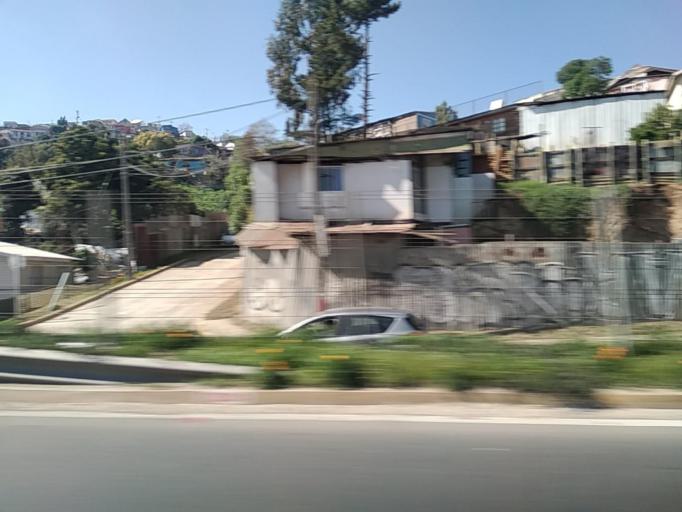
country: CL
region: Valparaiso
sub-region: Provincia de Valparaiso
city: Vina del Mar
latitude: -33.0162
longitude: -71.4998
